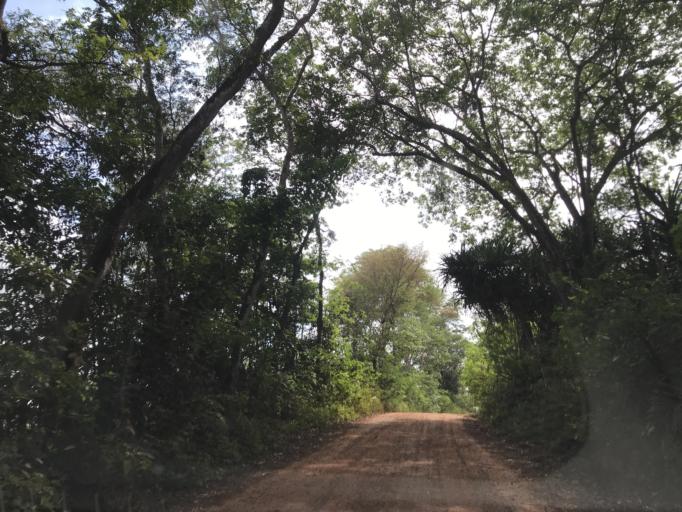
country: BR
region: Bahia
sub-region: Entre Rios
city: Entre Rios
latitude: -12.1720
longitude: -38.1402
